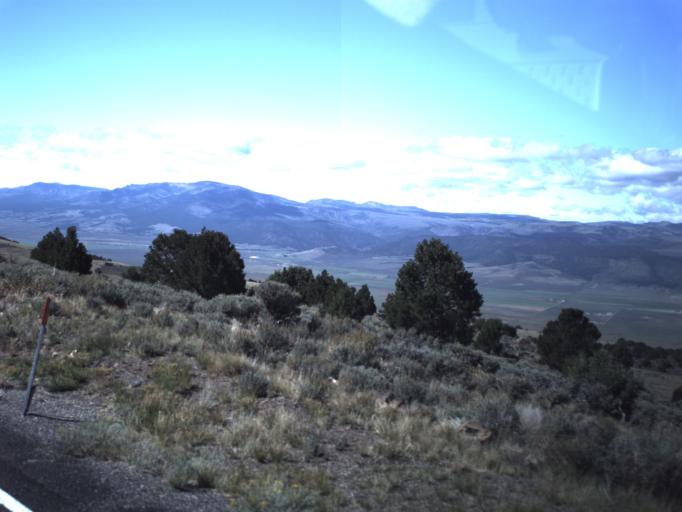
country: US
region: Utah
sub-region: Wayne County
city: Loa
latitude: 38.4776
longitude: -111.8295
